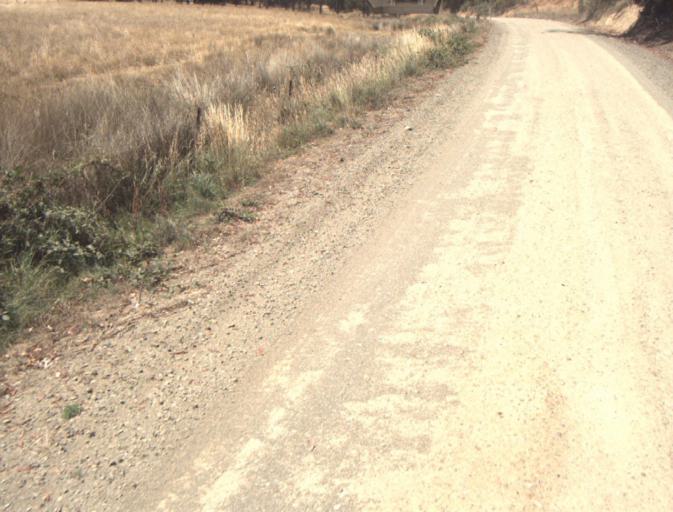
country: AU
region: Tasmania
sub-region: Dorset
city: Scottsdale
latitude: -41.2948
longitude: 147.3990
